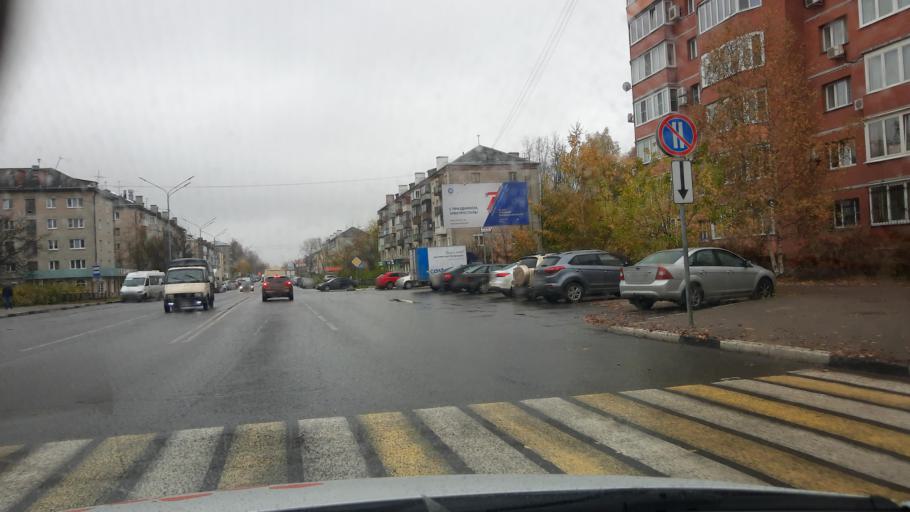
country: RU
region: Moskovskaya
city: Elektrostal'
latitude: 55.8013
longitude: 38.4374
